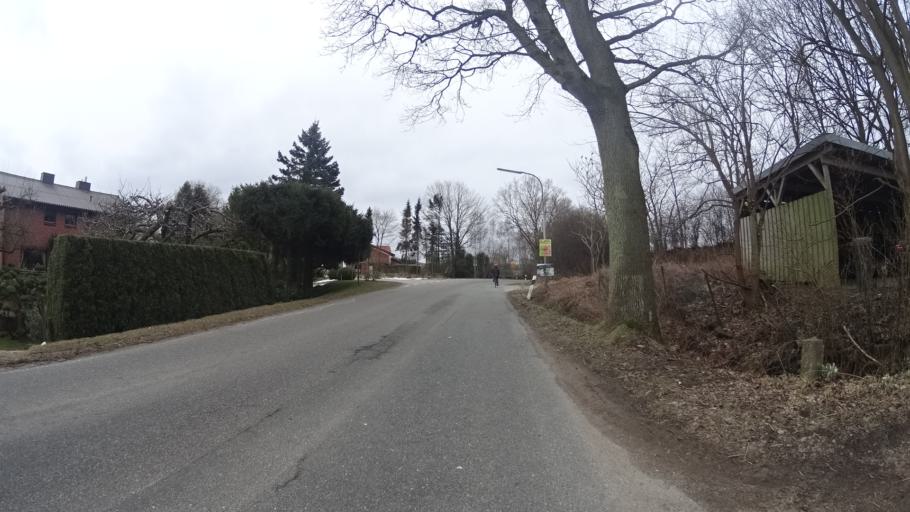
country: DE
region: Schleswig-Holstein
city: Neukirchen
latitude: 54.2113
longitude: 10.5557
